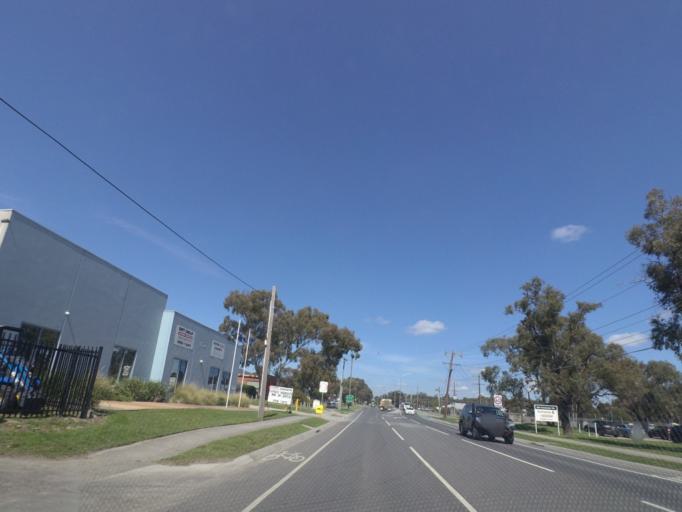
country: AU
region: Victoria
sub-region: Maroondah
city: Bayswater North
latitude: -37.8198
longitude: 145.3046
